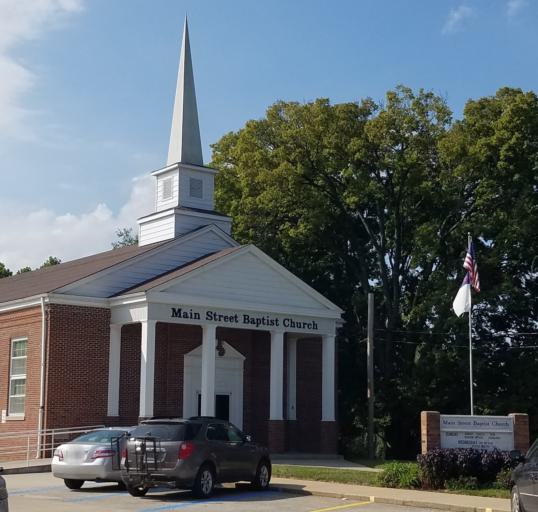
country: US
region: Missouri
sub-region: Moniteau County
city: California
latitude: 38.6362
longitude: -92.5678
